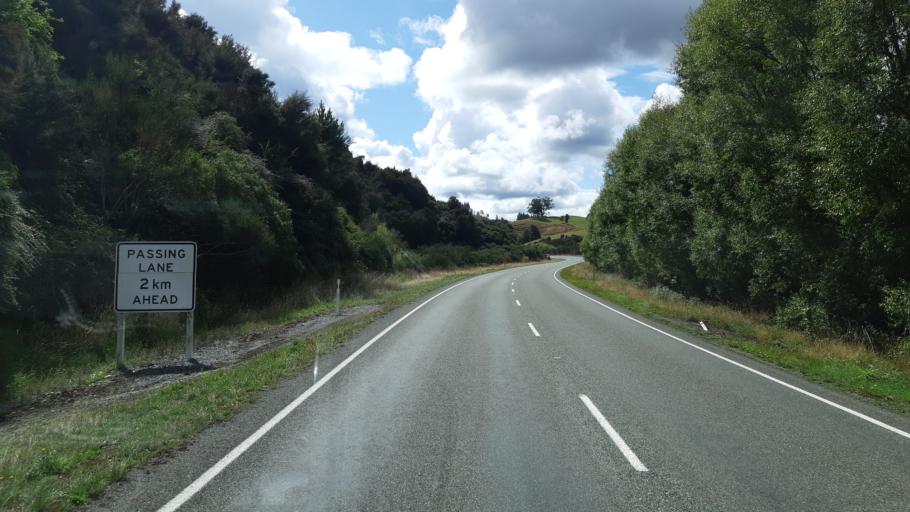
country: NZ
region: Tasman
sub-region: Tasman District
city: Wakefield
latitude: -41.6464
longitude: 172.6551
